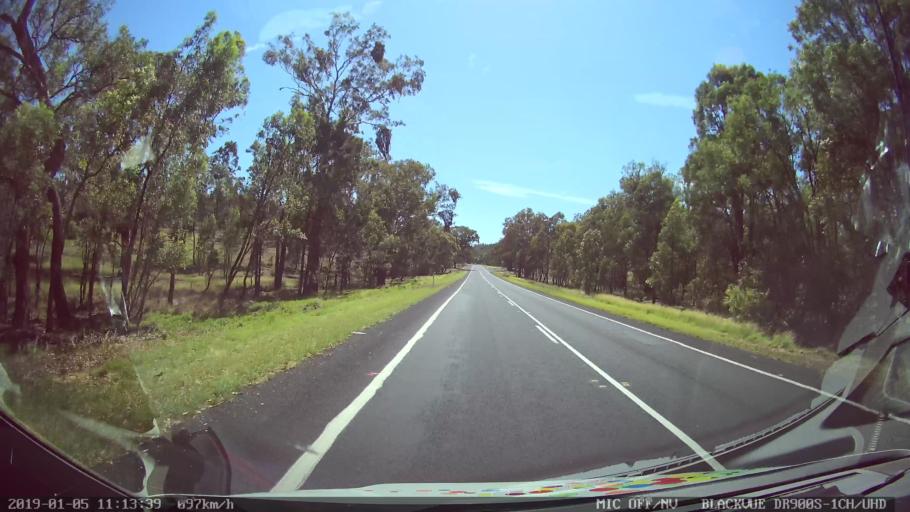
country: AU
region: New South Wales
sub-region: Warrumbungle Shire
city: Coonabarabran
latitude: -31.3696
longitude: 149.2741
